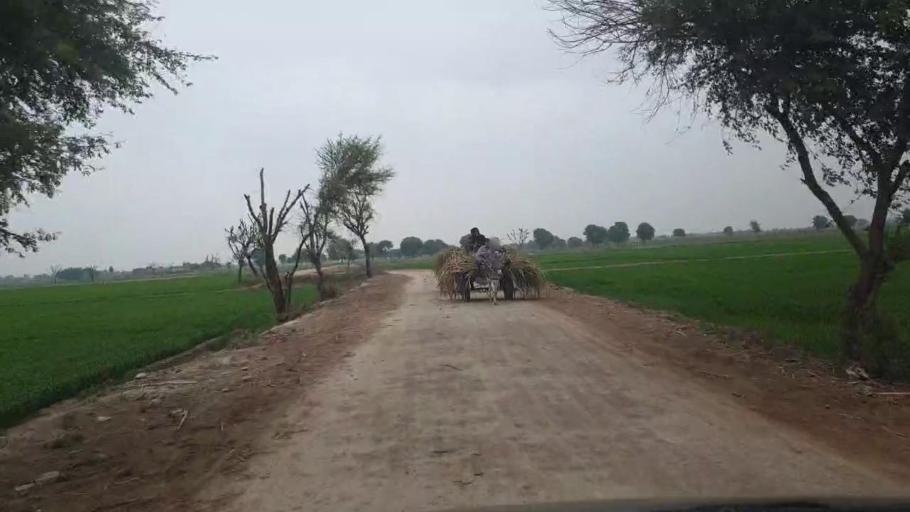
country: PK
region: Sindh
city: Shahdadpur
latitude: 25.9667
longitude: 68.7128
